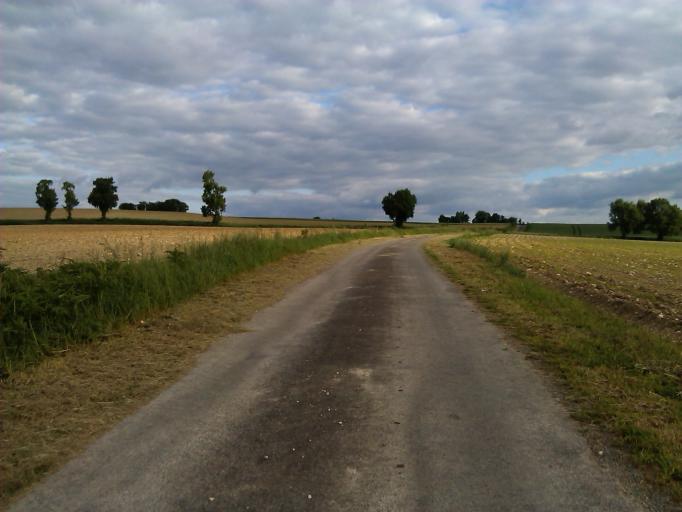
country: FR
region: Poitou-Charentes
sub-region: Departement de la Charente
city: Saint-Amant-de-Boixe
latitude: 45.7914
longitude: 0.1381
